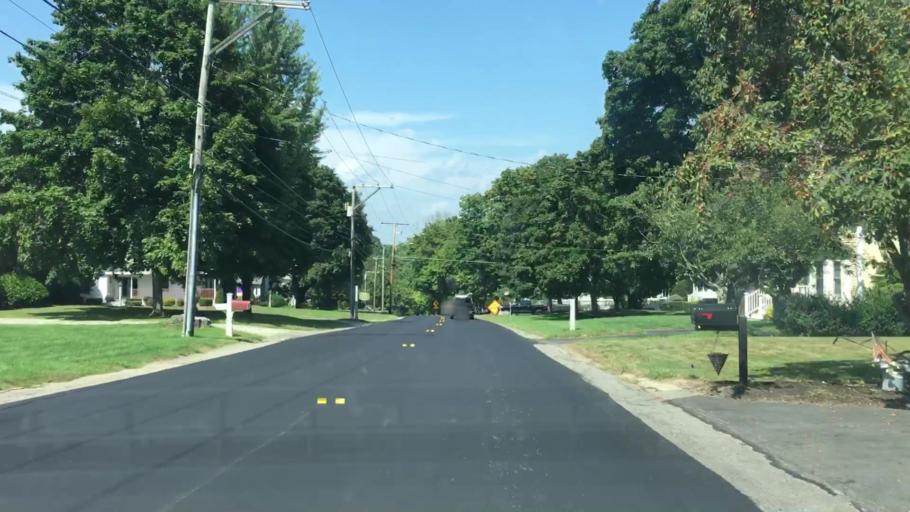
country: US
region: New Hampshire
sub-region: Rockingham County
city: Hampstead
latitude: 42.8815
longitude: -71.1869
